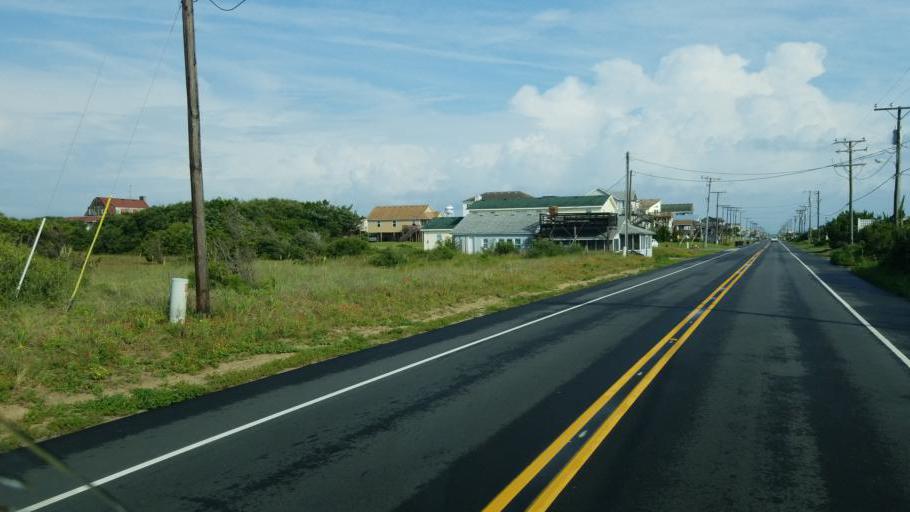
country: US
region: North Carolina
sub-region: Dare County
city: Kill Devil Hills
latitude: 36.0249
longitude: -75.6638
